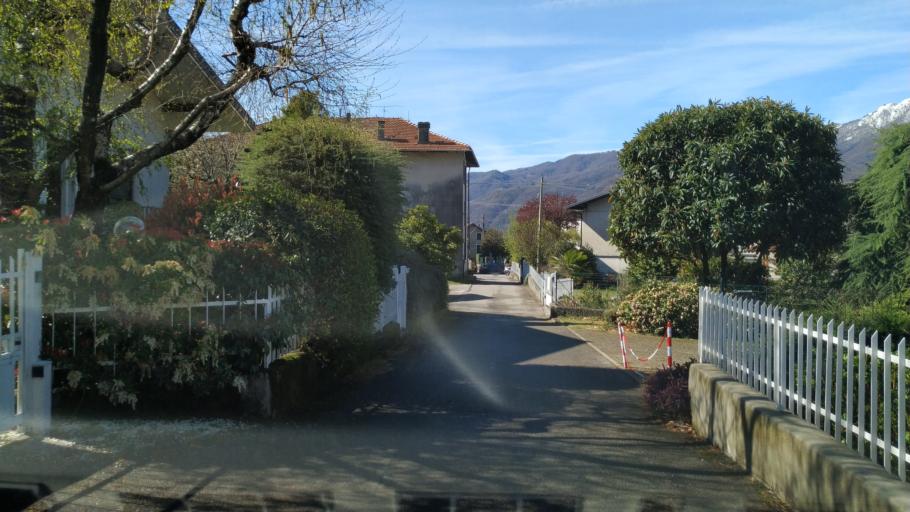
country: IT
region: Piedmont
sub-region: Provincia di Vercelli
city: Civiasco
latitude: 45.7929
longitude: 8.2777
